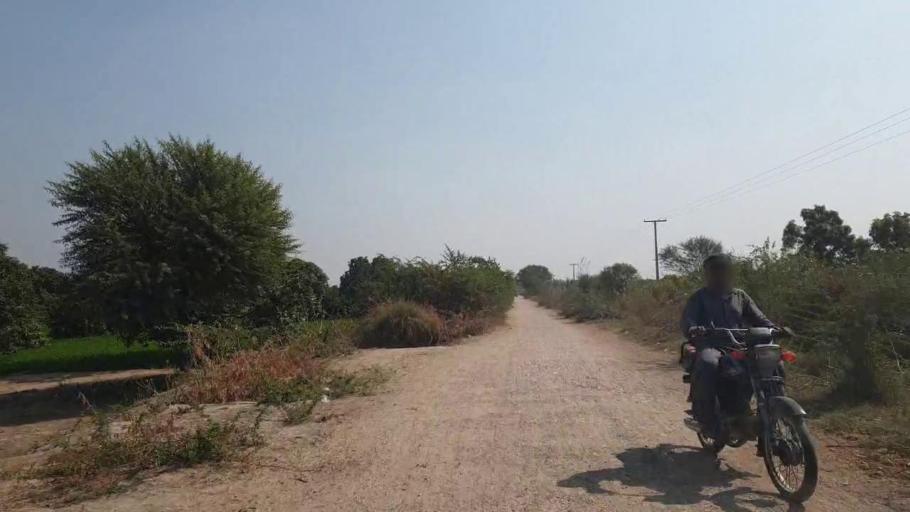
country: PK
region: Sindh
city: Chambar
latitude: 25.4107
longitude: 68.8999
